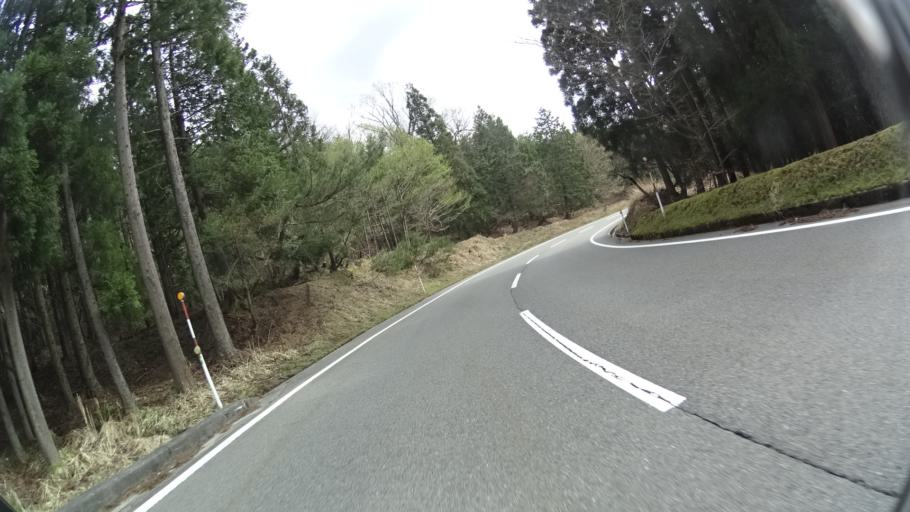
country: JP
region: Hyogo
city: Toyooka
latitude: 35.4974
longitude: 134.9175
